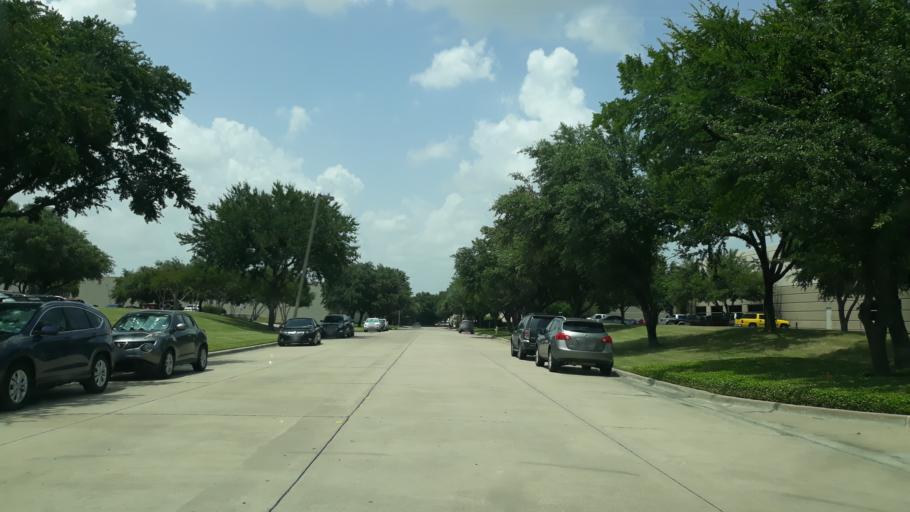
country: US
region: Texas
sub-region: Dallas County
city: Coppell
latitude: 32.9412
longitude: -97.0033
